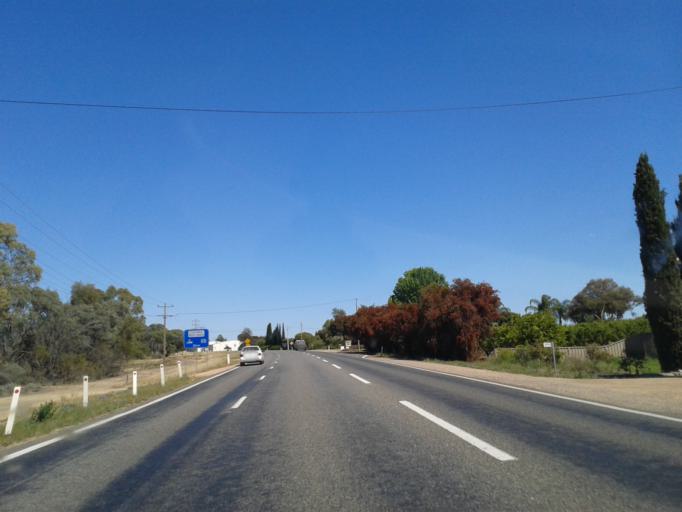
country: AU
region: New South Wales
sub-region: Wentworth
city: Dareton
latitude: -34.1107
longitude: 141.9822
